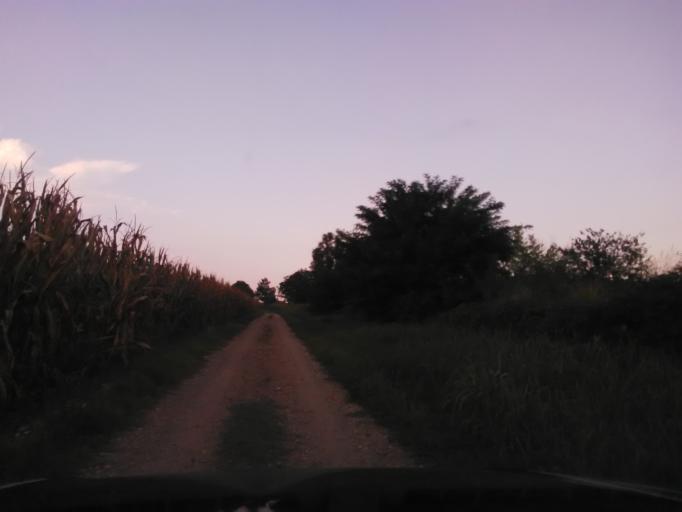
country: IT
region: Piedmont
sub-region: Provincia di Vercelli
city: Cigliano
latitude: 45.3079
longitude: 8.0428
